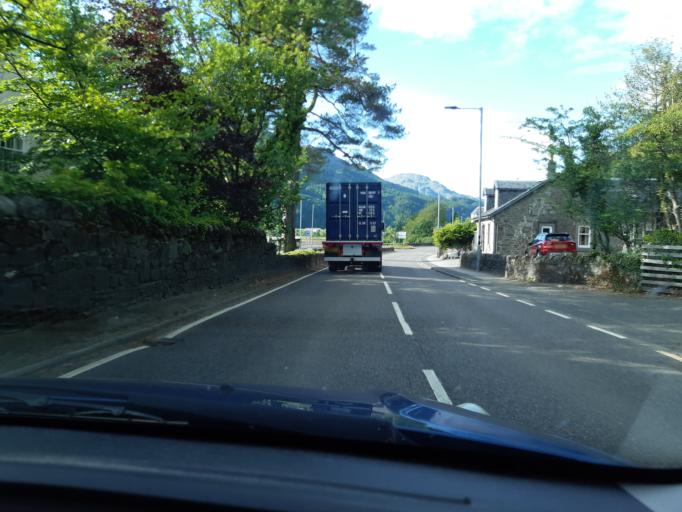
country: GB
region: Scotland
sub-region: Argyll and Bute
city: Garelochhead
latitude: 56.1999
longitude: -4.7456
